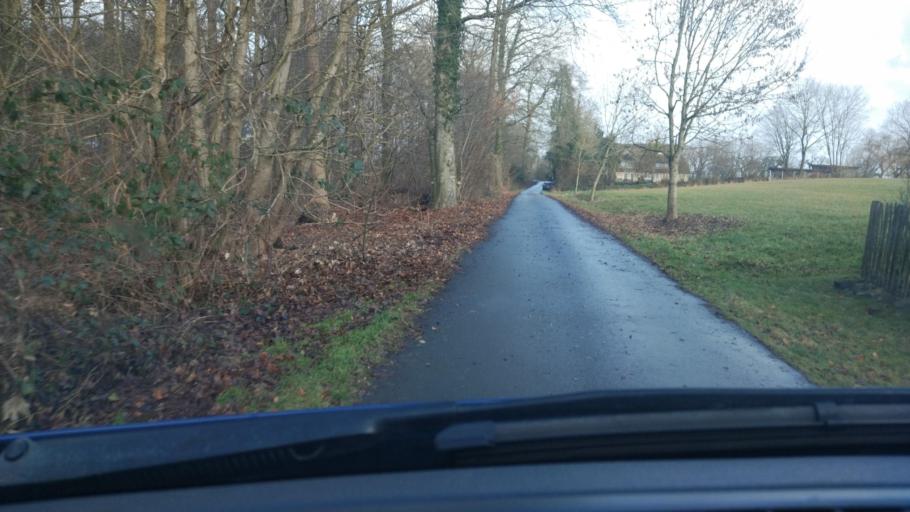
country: DE
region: Schleswig-Holstein
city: Taarstedt
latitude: 54.5550
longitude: 9.6830
